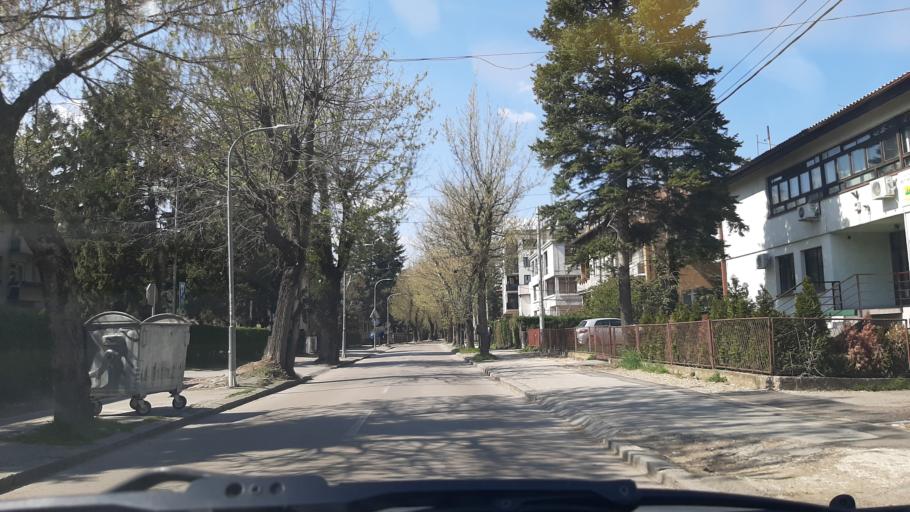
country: BA
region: Republika Srpska
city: Banja Luka
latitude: 44.7741
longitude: 17.1858
